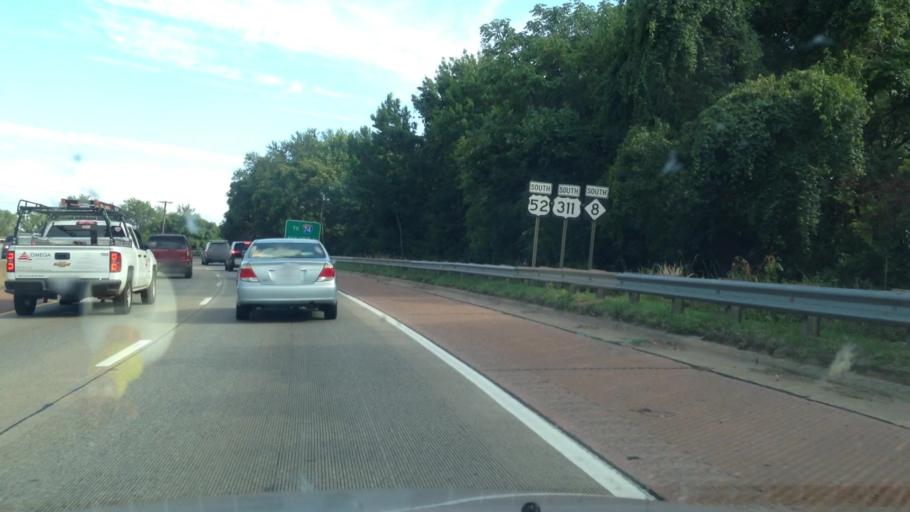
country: US
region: North Carolina
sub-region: Forsyth County
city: Winston-Salem
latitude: 36.0750
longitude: -80.2306
